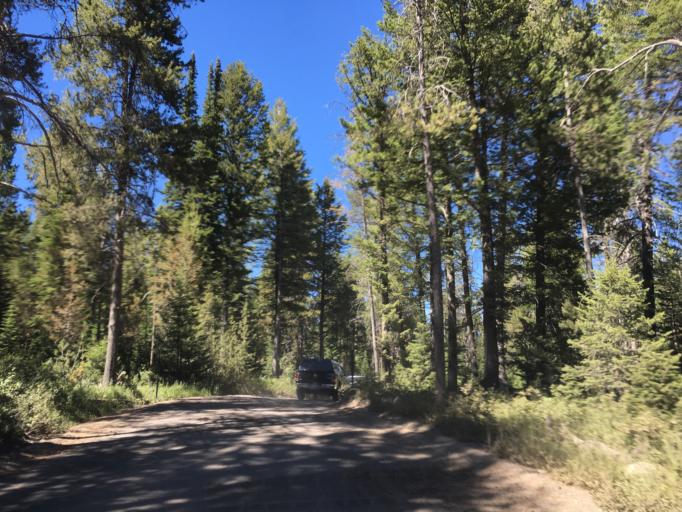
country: US
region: Wyoming
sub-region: Teton County
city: Moose Wilson Road
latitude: 43.6161
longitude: -110.7910
